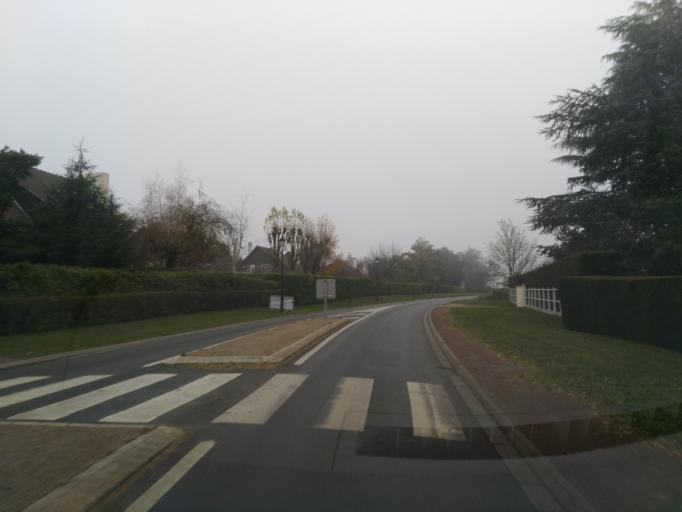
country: FR
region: Ile-de-France
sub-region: Departement des Yvelines
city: Chavenay
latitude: 48.8532
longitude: 1.9926
